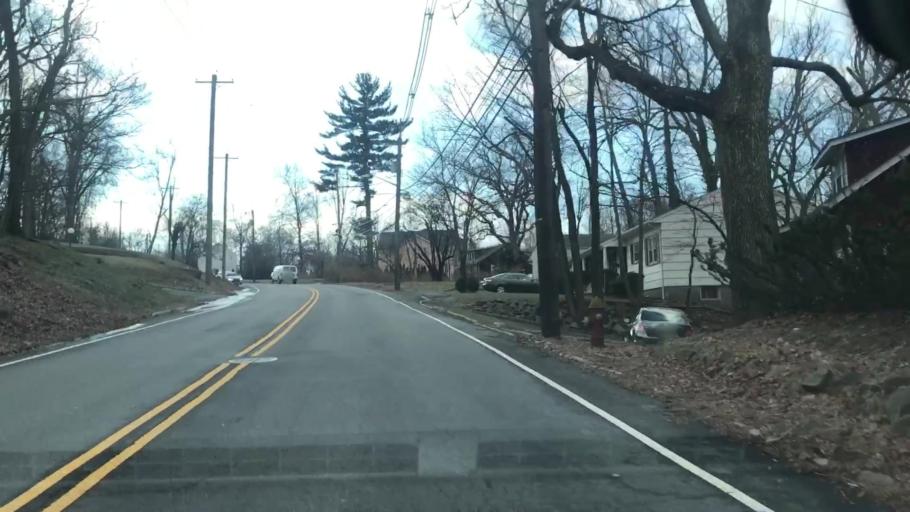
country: US
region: New Jersey
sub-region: Essex County
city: Livingston
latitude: 40.7767
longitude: -74.3008
